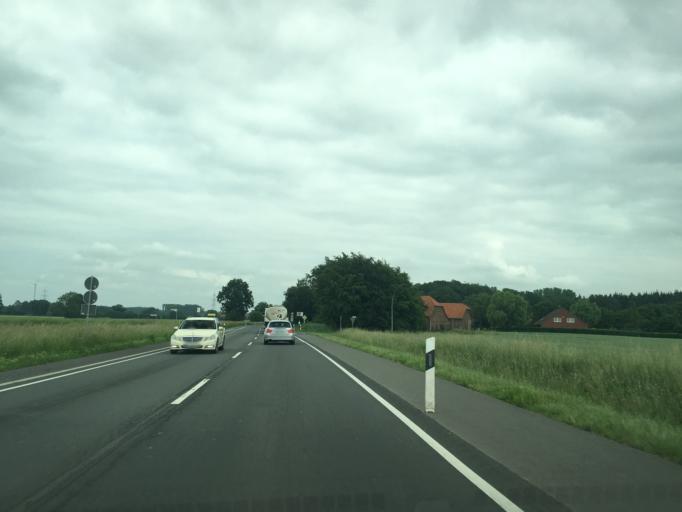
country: DE
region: North Rhine-Westphalia
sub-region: Regierungsbezirk Munster
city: Laer
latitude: 52.0542
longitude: 7.3977
